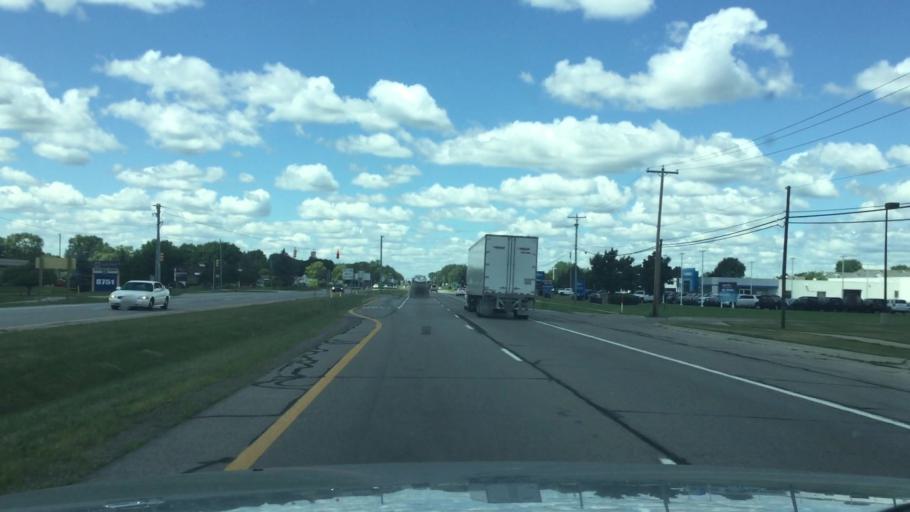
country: US
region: Michigan
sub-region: Saginaw County
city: Shields
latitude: 43.4161
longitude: -84.0852
